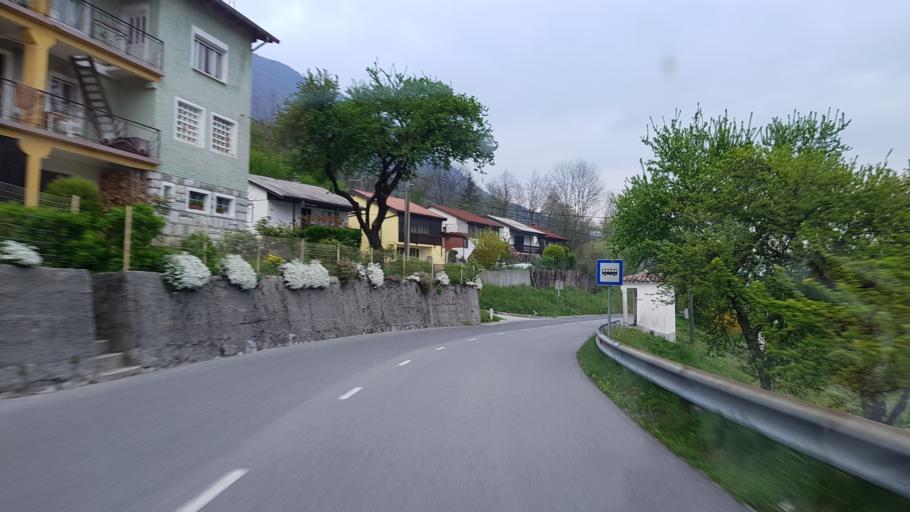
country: IT
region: Friuli Venezia Giulia
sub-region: Provincia di Udine
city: Pulfero
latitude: 46.2555
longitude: 13.4902
